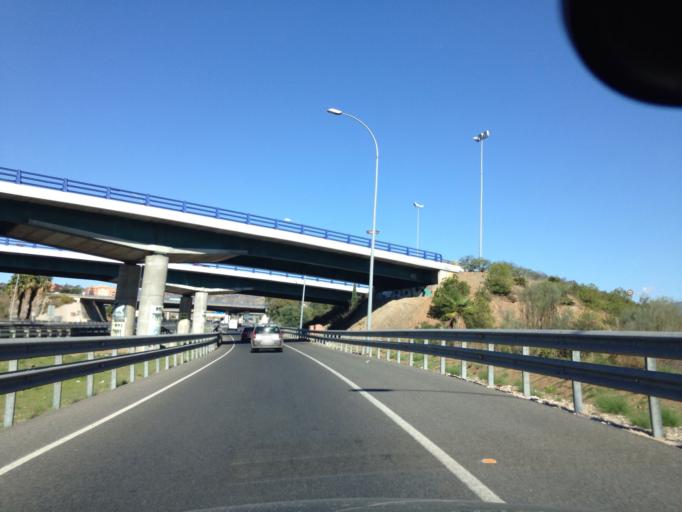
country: ES
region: Andalusia
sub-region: Provincia de Malaga
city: Malaga
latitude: 36.7109
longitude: -4.4576
